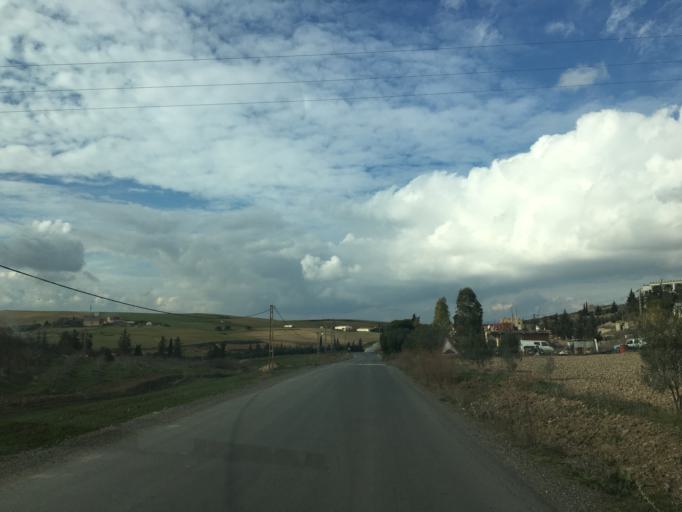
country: DZ
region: Bouira
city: Bouira
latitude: 36.2916
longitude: 3.8488
